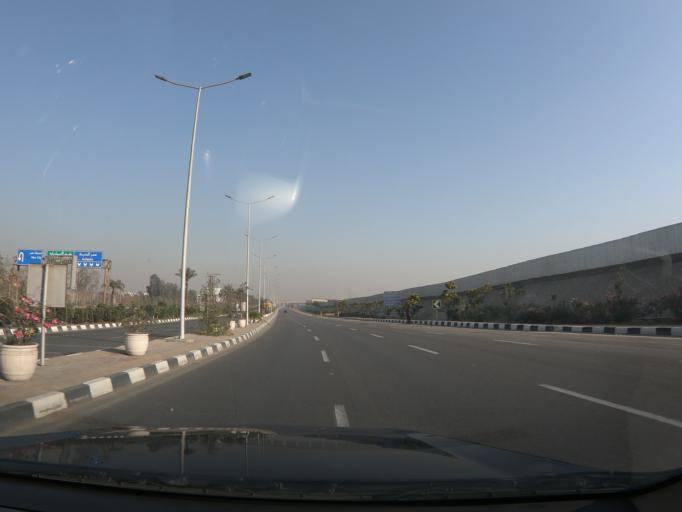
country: EG
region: Muhafazat al Qalyubiyah
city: Al Khankah
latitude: 30.1047
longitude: 31.3877
